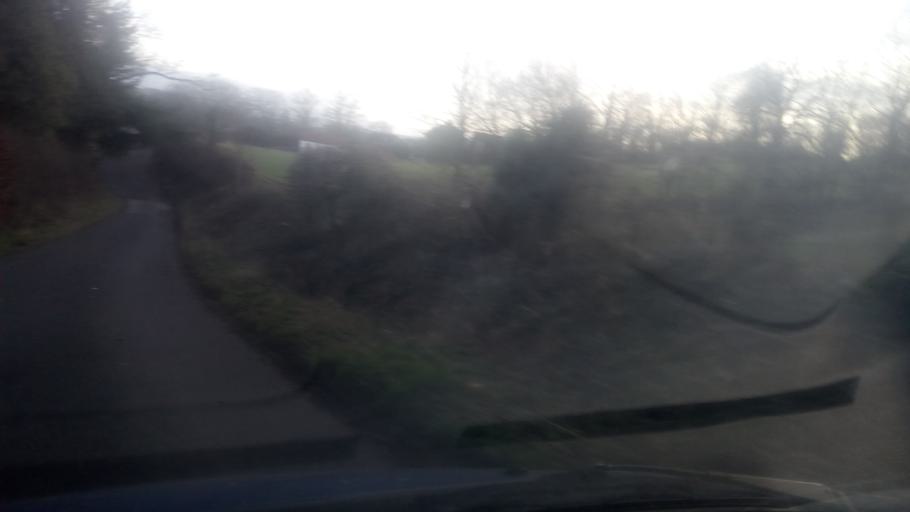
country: GB
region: Scotland
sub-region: The Scottish Borders
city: Jedburgh
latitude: 55.4863
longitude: -2.5522
